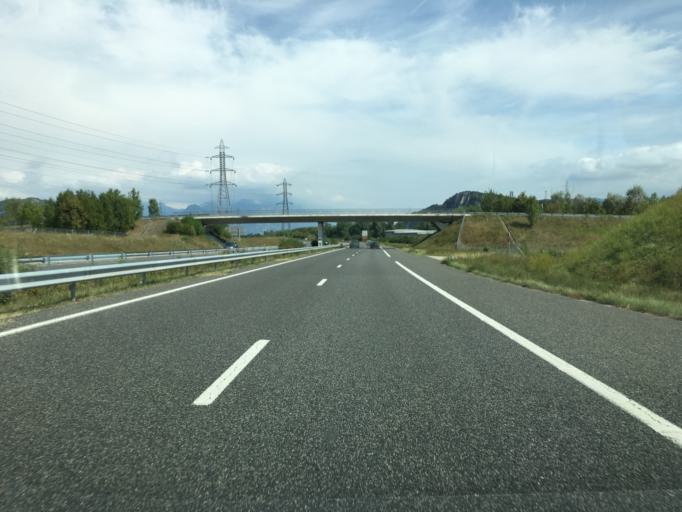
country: FR
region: Rhone-Alpes
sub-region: Departement de l'Isere
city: Allieres-et-Risset
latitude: 45.0969
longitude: 5.6722
